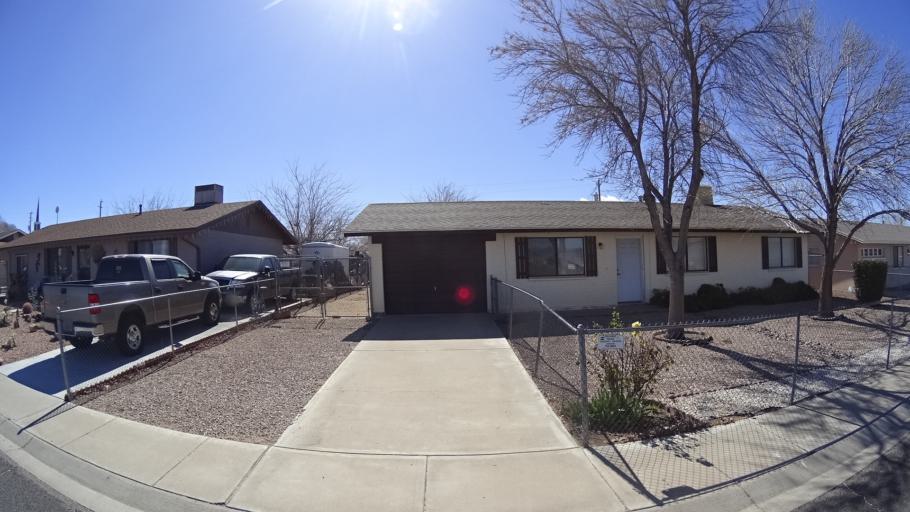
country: US
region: Arizona
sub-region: Mohave County
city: Kingman
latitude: 35.1958
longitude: -114.0124
